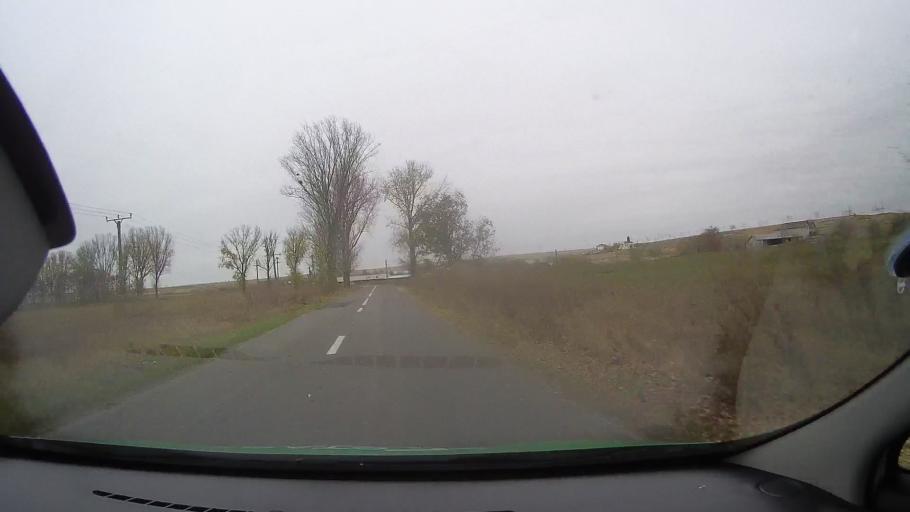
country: RO
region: Constanta
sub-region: Comuna Saraiu
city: Saraiu
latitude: 44.7252
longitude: 28.2206
